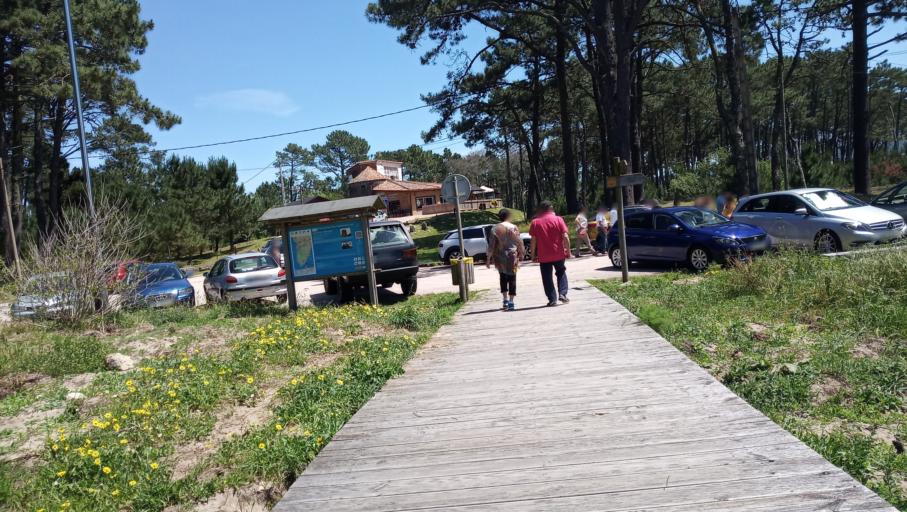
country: ES
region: Galicia
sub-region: Provincia de Pontevedra
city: A Guarda
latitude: 41.8735
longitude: -8.8696
